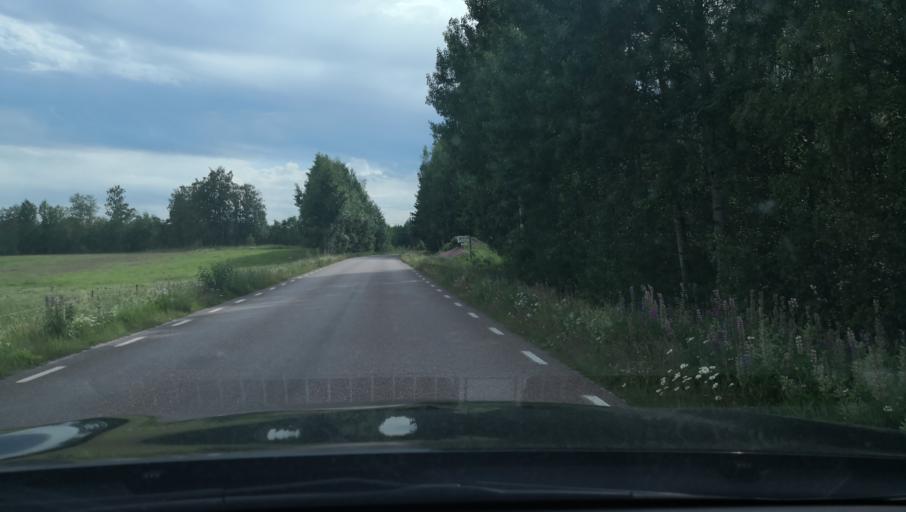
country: SE
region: Dalarna
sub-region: Smedjebackens Kommun
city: Smedjebacken
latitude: 60.0490
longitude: 15.5513
